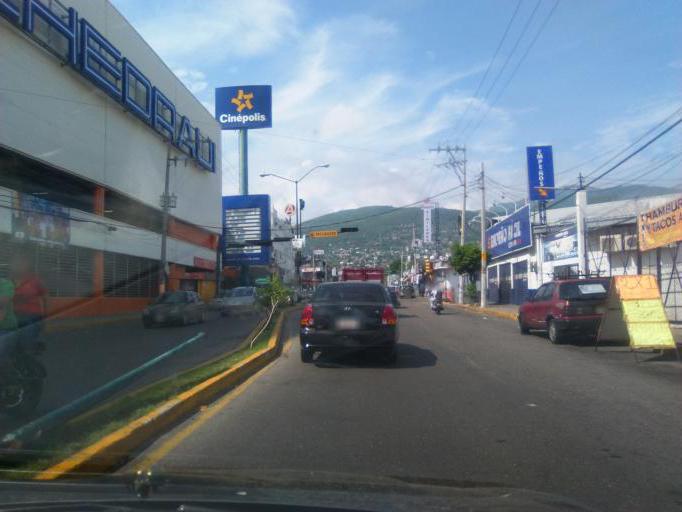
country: MX
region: Guerrero
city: Acapulco de Juarez
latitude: 16.8578
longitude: -99.9150
